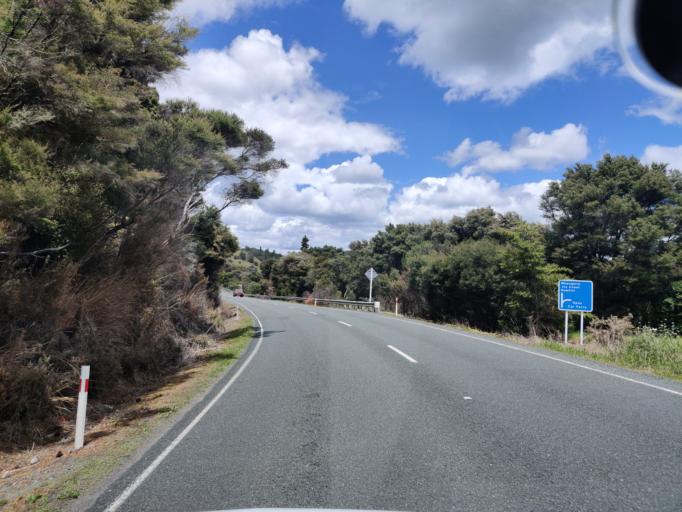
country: NZ
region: Northland
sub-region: Far North District
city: Paihia
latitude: -35.2849
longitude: 174.1474
